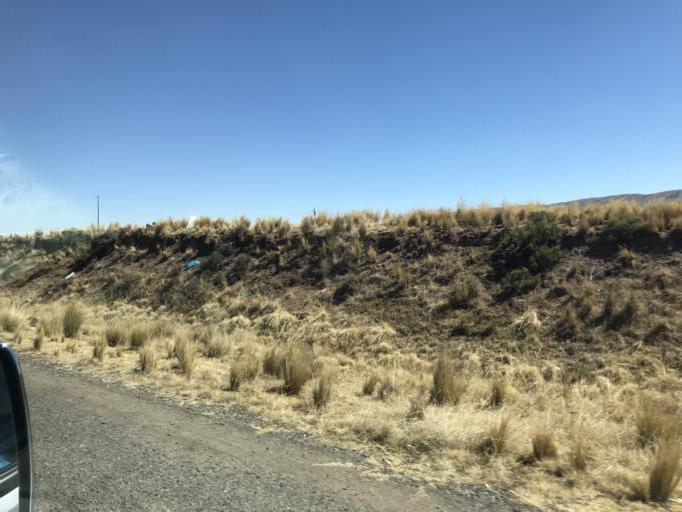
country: BO
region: La Paz
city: Tiahuanaco
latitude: -16.5701
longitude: -68.6671
